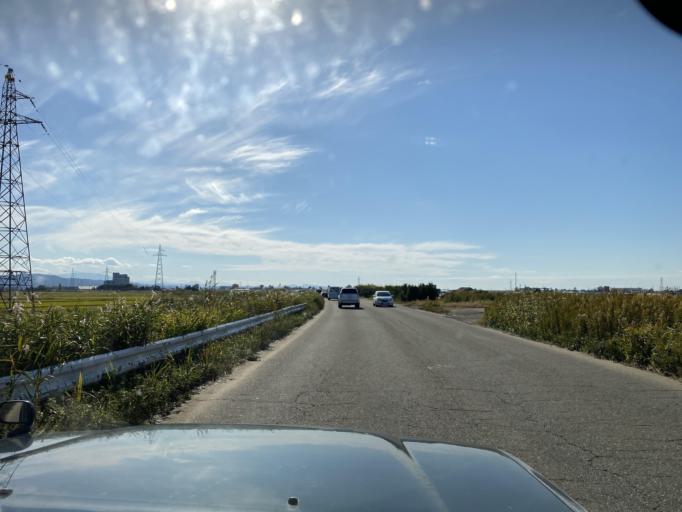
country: JP
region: Niigata
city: Niitsu-honcho
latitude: 37.8028
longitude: 139.0775
